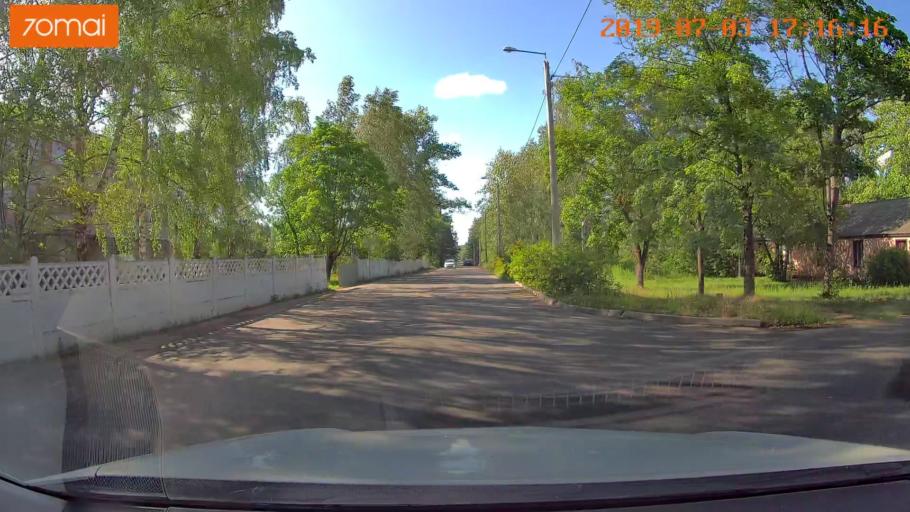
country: BY
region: Minsk
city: Vyaliki Trastsyanets
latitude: 53.9056
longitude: 27.6779
